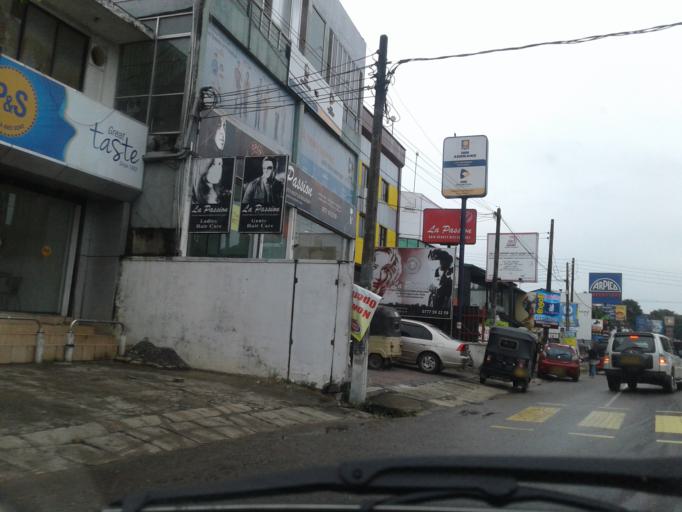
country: LK
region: Western
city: Battaramulla South
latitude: 6.9062
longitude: 79.9475
